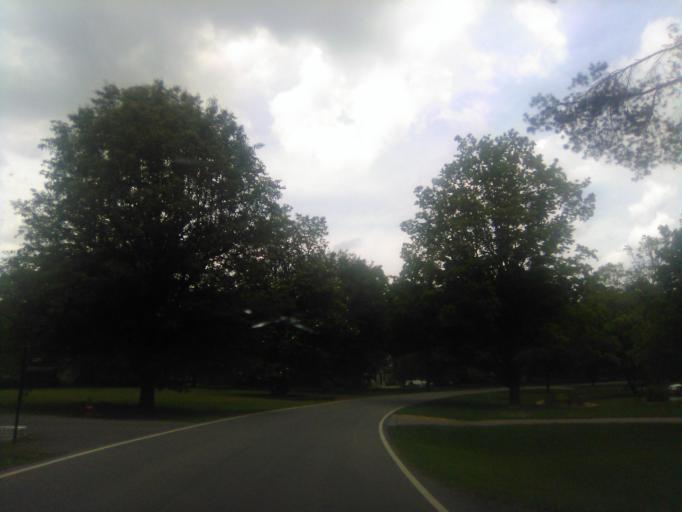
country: US
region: Tennessee
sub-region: Davidson County
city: Belle Meade
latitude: 36.0816
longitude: -86.8642
